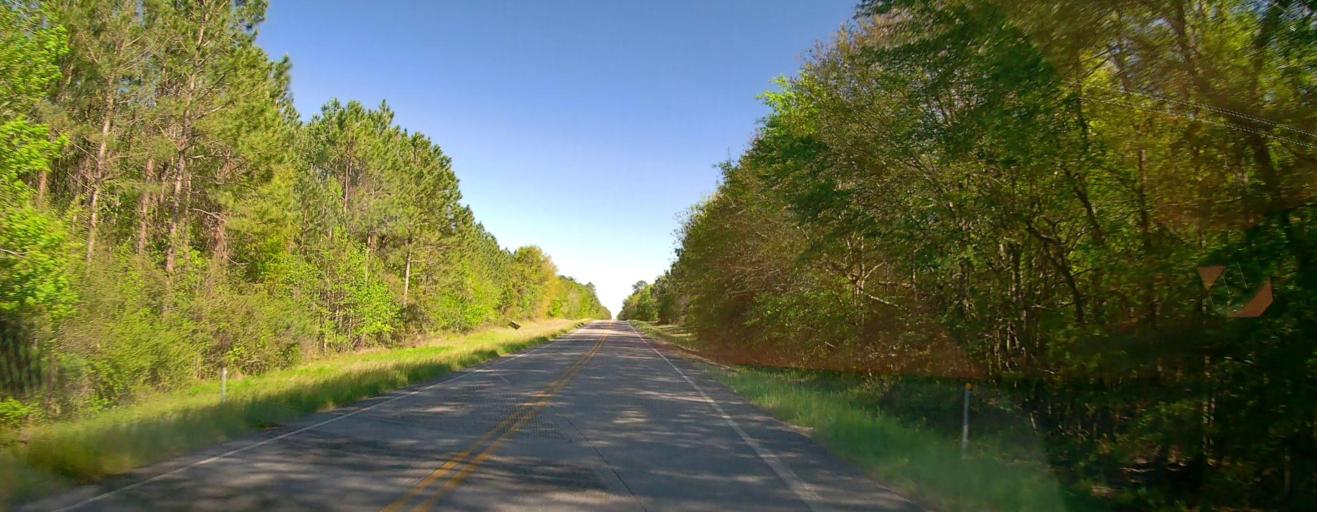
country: US
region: Georgia
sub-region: Wilcox County
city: Rochelle
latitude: 32.0107
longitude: -83.4921
